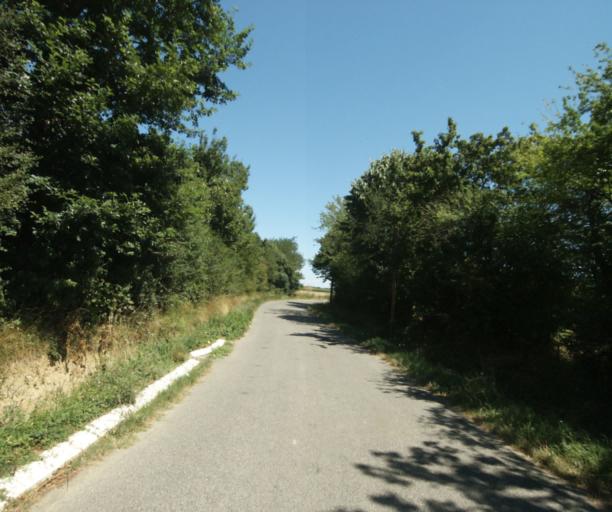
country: FR
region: Midi-Pyrenees
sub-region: Departement de la Haute-Garonne
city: Saint-Felix-Lauragais
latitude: 43.4588
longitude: 1.9446
